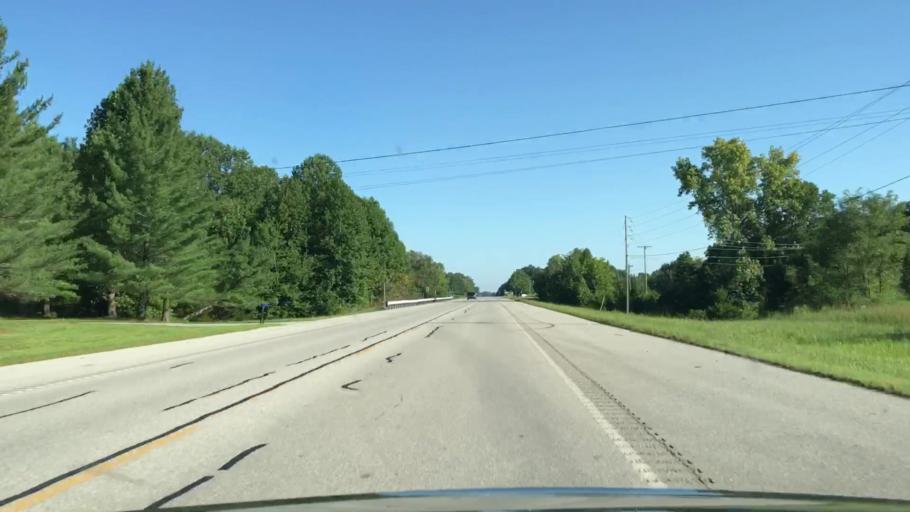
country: US
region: Tennessee
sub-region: Putnam County
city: Baxter
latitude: 36.2126
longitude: -85.6129
